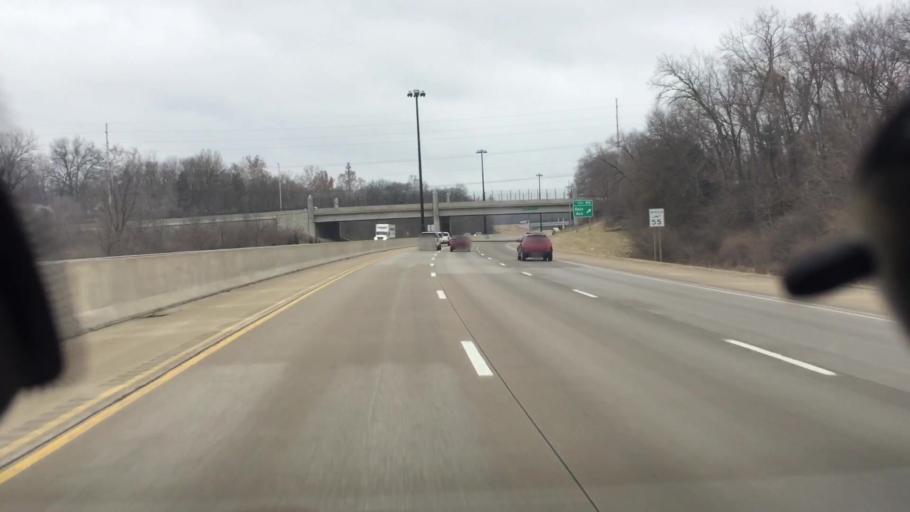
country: US
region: Illinois
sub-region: Peoria County
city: West Peoria
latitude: 40.7268
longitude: -89.6200
